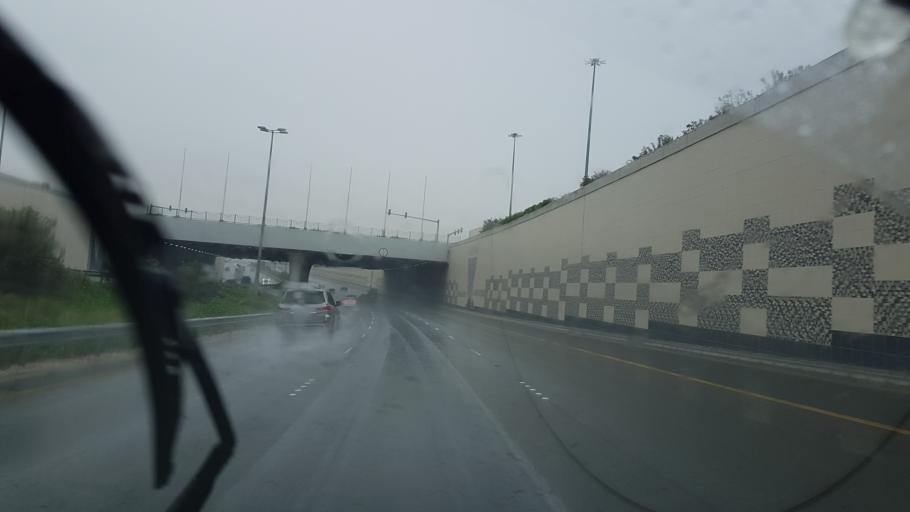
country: BH
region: Central Governorate
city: Madinat Hamad
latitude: 26.1226
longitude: 50.5067
